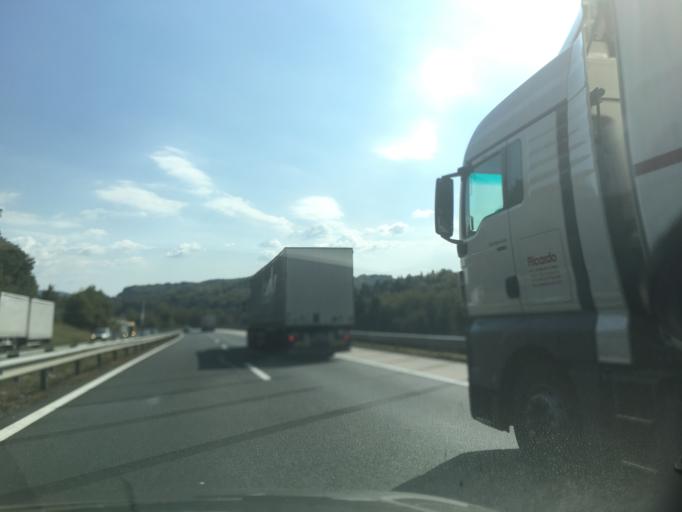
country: SI
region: Ivancna Gorica
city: Sentvid pri Sticni
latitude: 45.9279
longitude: 14.9293
